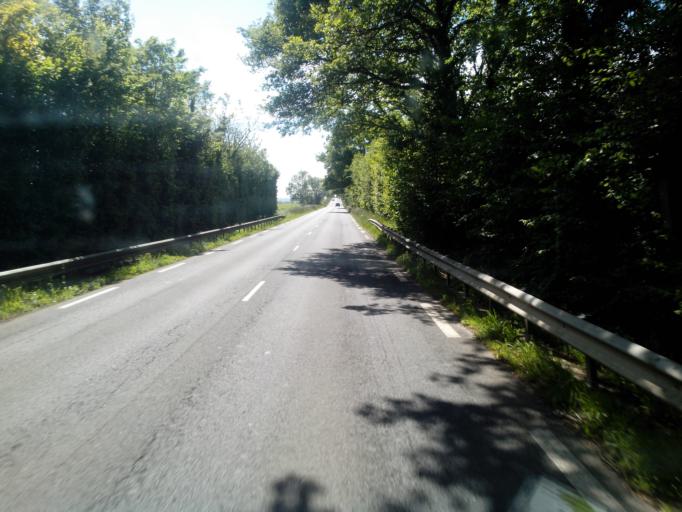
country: FR
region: Lower Normandy
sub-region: Departement du Calvados
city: Saint-Gatien-des-Bois
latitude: 49.3025
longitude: 0.2444
